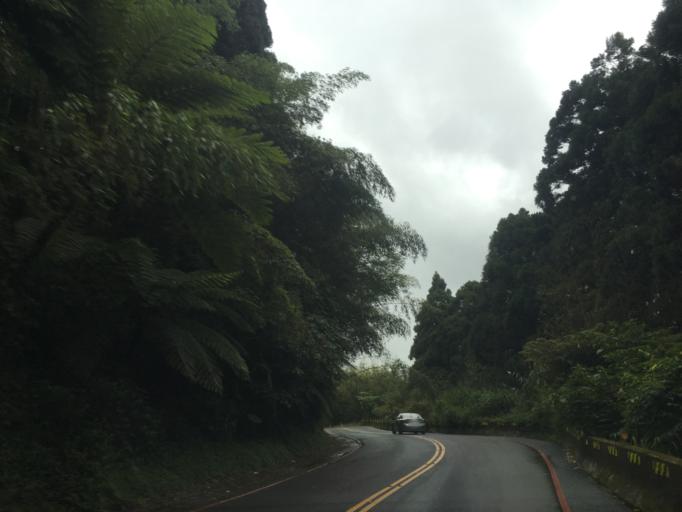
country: TW
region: Taiwan
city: Lugu
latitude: 23.5033
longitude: 120.6984
